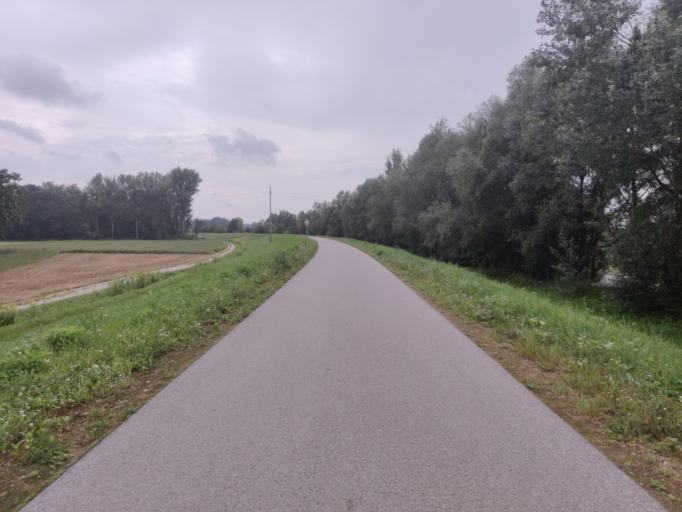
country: AT
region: Lower Austria
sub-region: Politischer Bezirk Amstetten
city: Ennsdorf
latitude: 48.2355
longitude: 14.5655
